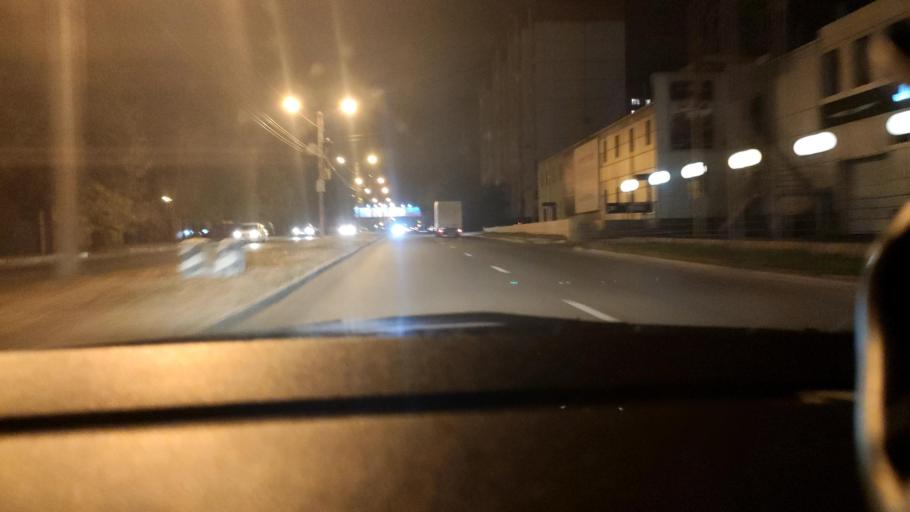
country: RU
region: Voronezj
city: Voronezh
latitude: 51.7062
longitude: 39.1956
